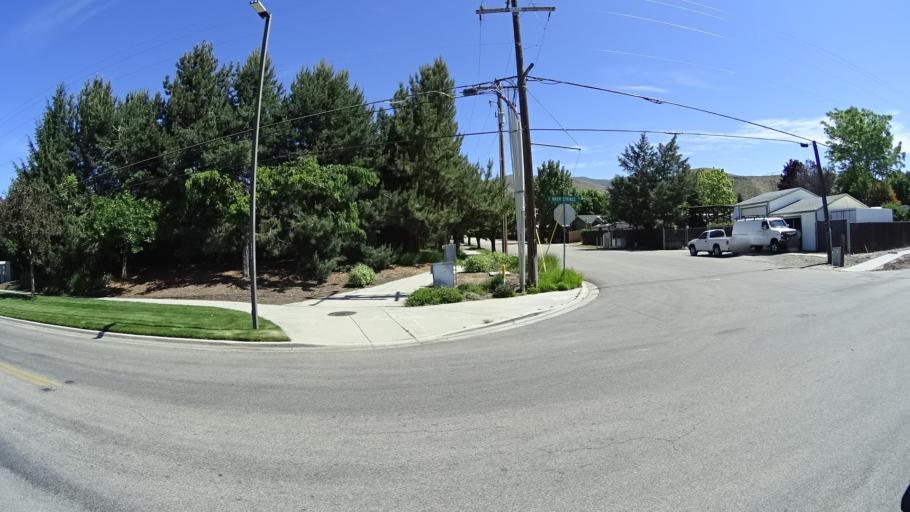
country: US
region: Idaho
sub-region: Ada County
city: Boise
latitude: 43.5679
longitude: -116.1187
